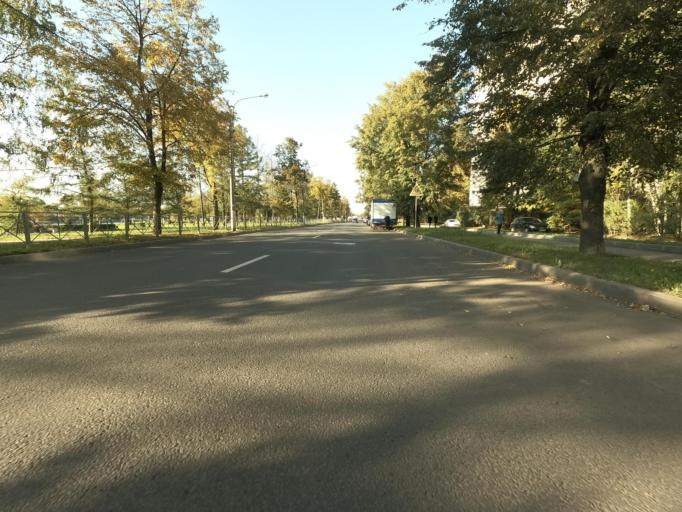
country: RU
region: St.-Petersburg
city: Kolpino
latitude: 59.7437
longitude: 30.6025
